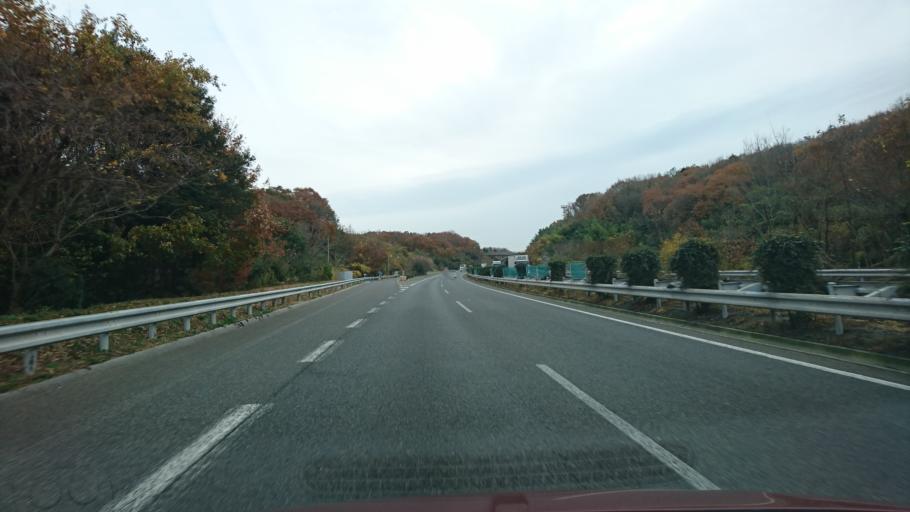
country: JP
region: Hyogo
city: Miki
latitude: 34.8212
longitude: 135.1033
